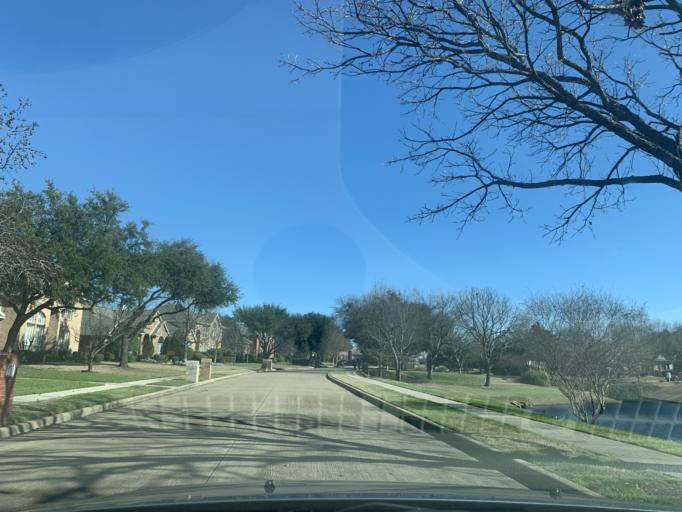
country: US
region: Texas
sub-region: Denton County
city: The Colony
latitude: 33.0619
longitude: -96.8355
